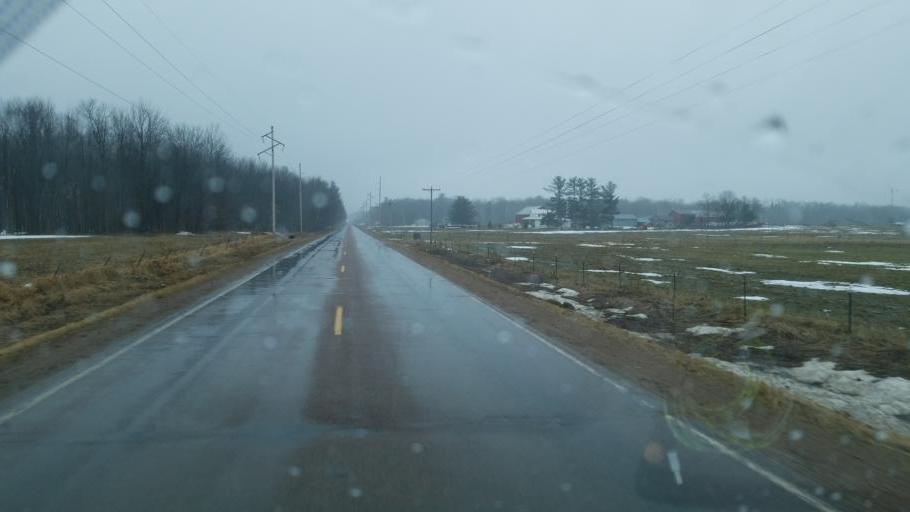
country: US
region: Wisconsin
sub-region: Clark County
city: Neillsville
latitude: 44.5295
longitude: -90.3963
